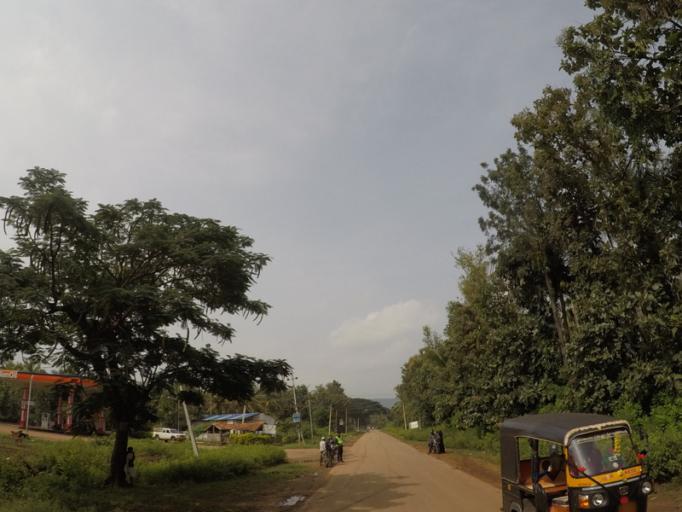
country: IN
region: Karnataka
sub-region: Chikmagalur
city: Tarikere
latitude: 13.5934
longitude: 75.8383
